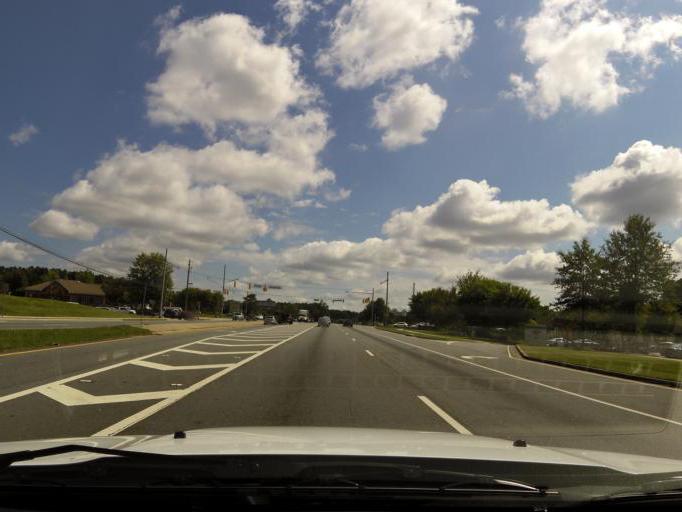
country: US
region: Georgia
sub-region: Cobb County
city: Kennesaw
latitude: 34.0225
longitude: -84.6266
